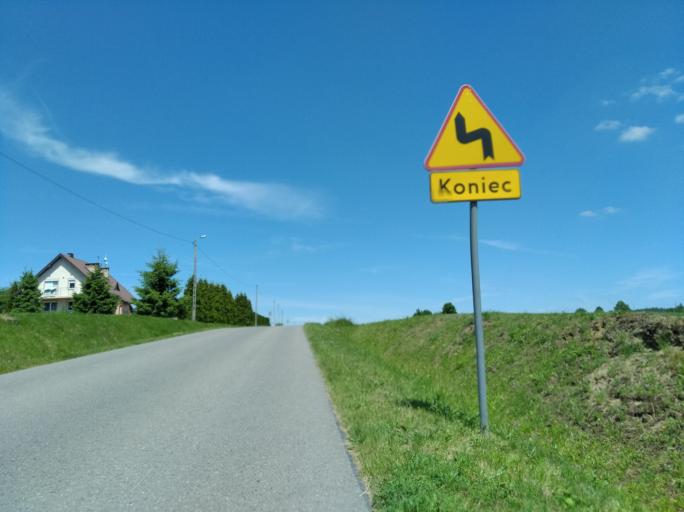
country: PL
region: Subcarpathian Voivodeship
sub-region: Powiat jasielski
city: Osiek Jasielski
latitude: 49.6680
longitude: 21.5440
